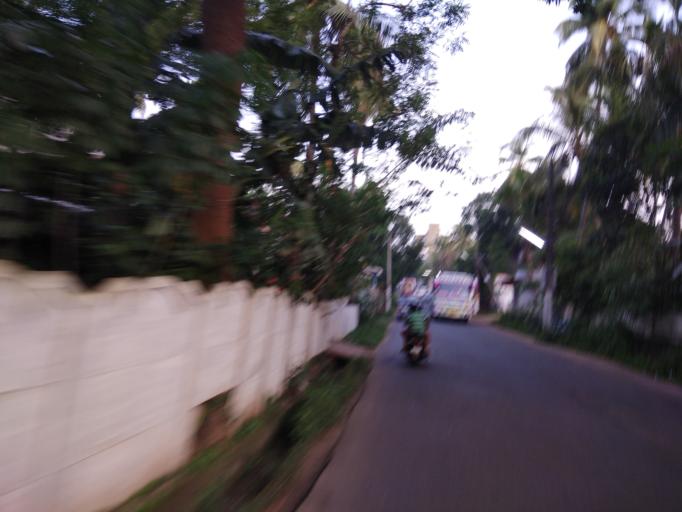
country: IN
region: Kerala
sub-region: Thrissur District
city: Trichur
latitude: 10.5342
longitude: 76.1837
